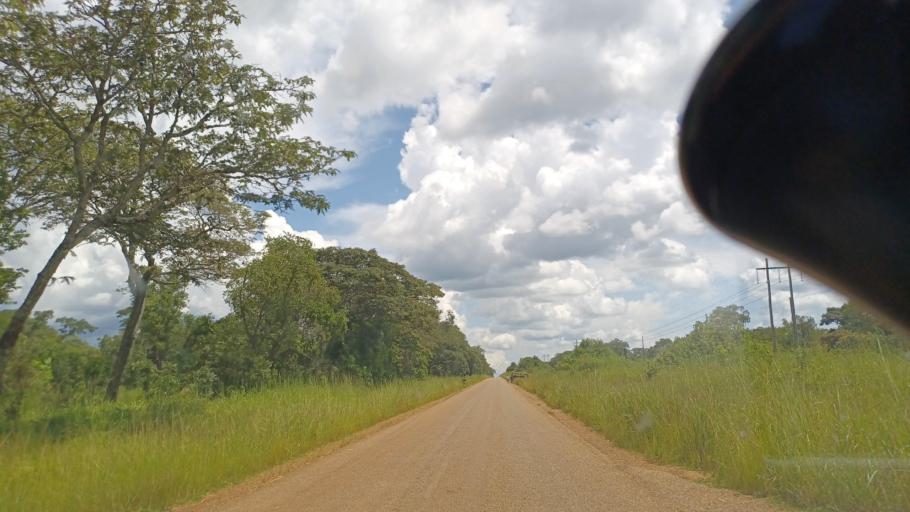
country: ZM
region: North-Western
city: Solwezi
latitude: -12.7013
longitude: 26.0352
